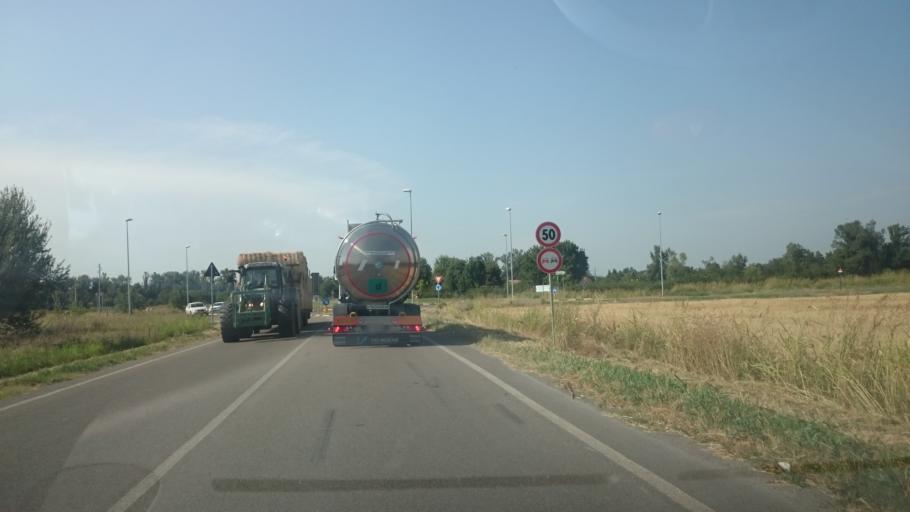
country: IT
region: Emilia-Romagna
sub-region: Provincia di Reggio Emilia
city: Fellegara
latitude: 44.6041
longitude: 10.7048
